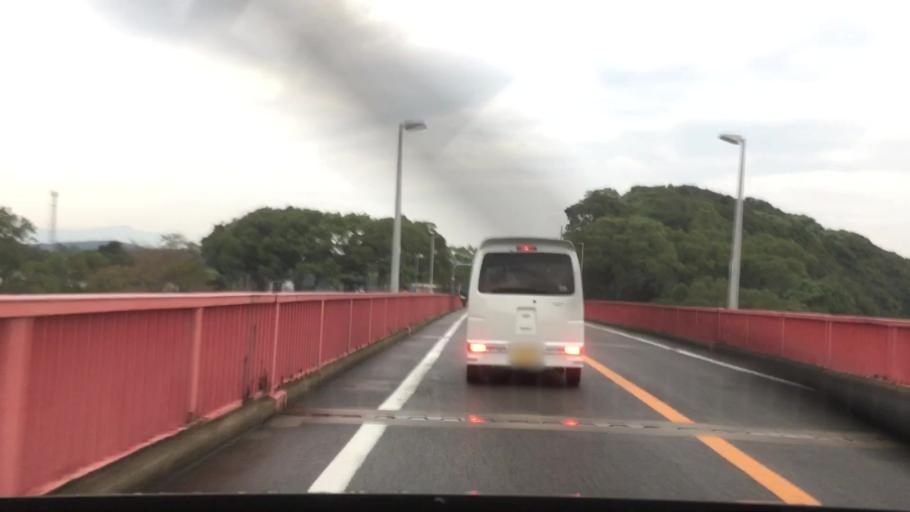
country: JP
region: Nagasaki
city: Sasebo
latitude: 33.0535
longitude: 129.7582
